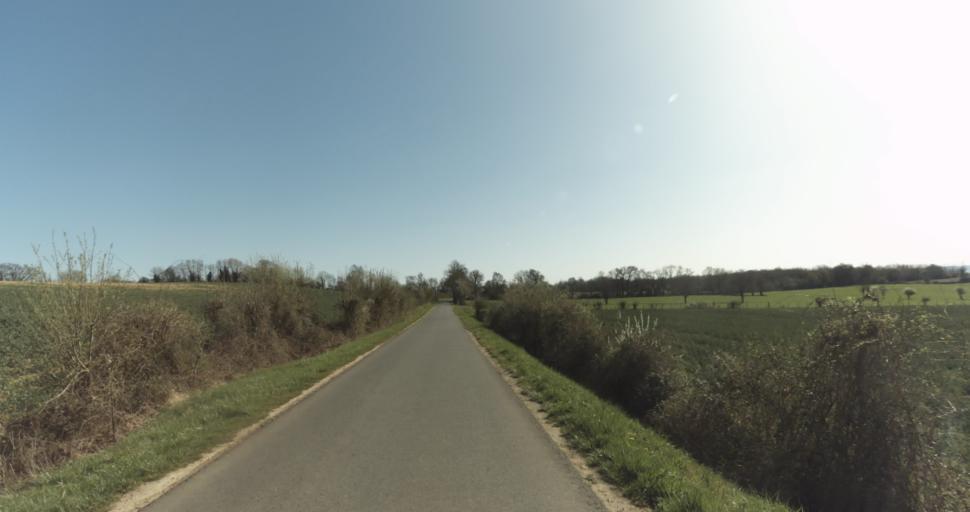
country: FR
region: Lower Normandy
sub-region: Departement de l'Orne
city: Trun
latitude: 48.8996
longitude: 0.0327
